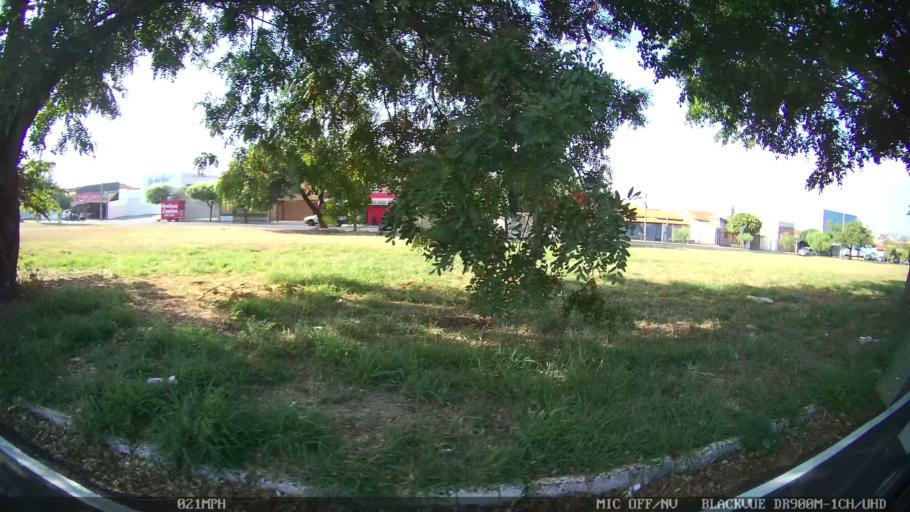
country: BR
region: Sao Paulo
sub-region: Sao Jose Do Rio Preto
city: Sao Jose do Rio Preto
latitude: -20.7861
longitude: -49.4098
